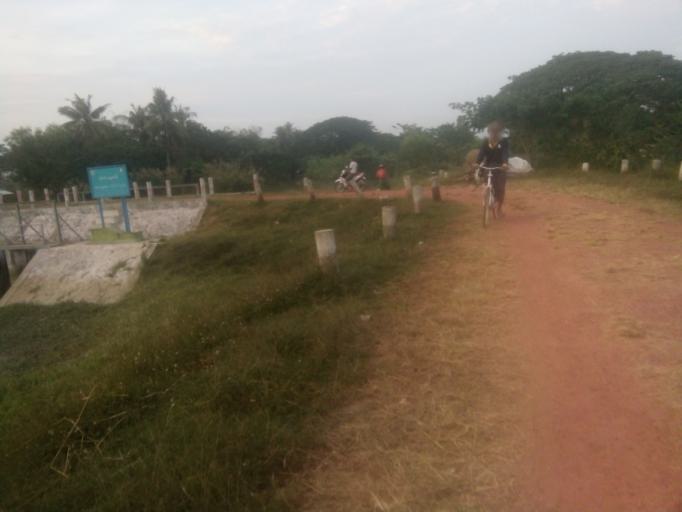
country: MM
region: Yangon
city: Kanbe
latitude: 16.8799
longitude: 95.9753
